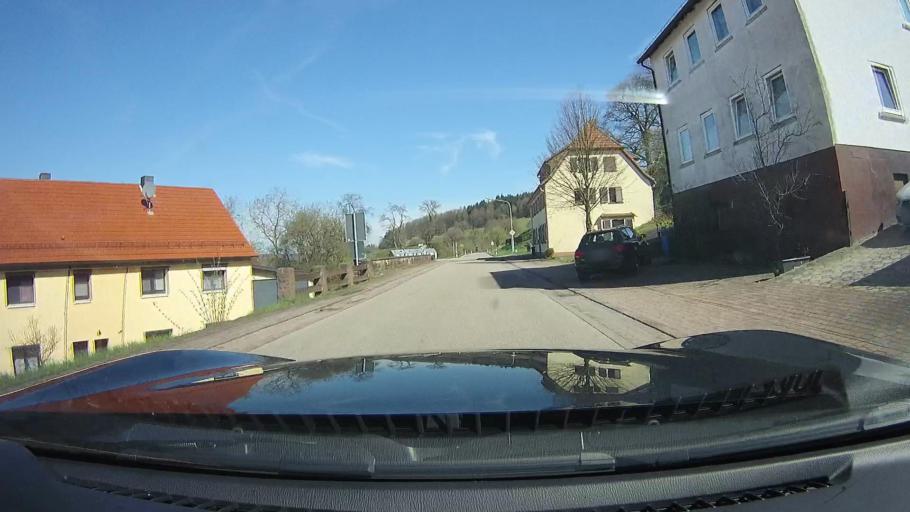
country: DE
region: Hesse
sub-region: Regierungsbezirk Darmstadt
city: Rothenberg
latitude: 49.5001
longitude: 8.9187
